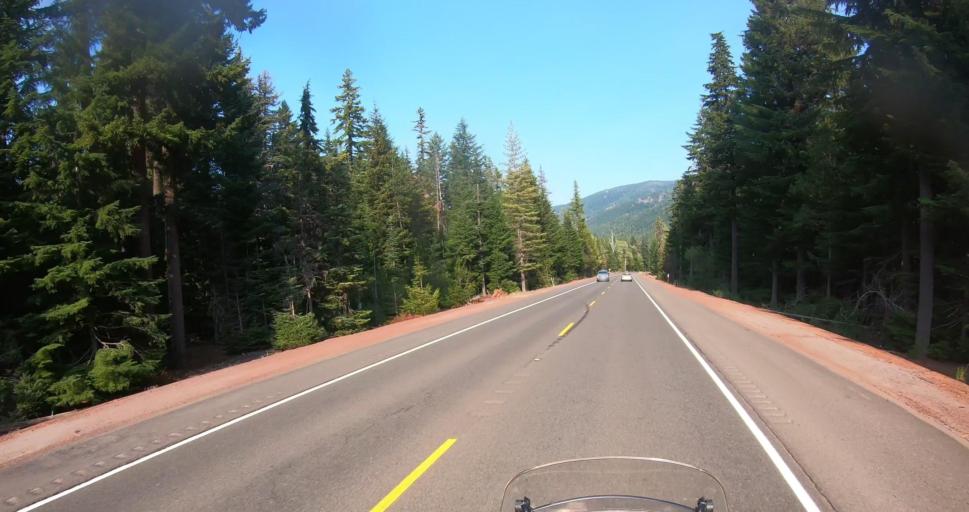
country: US
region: Oregon
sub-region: Hood River County
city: Odell
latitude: 45.3303
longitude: -121.5848
